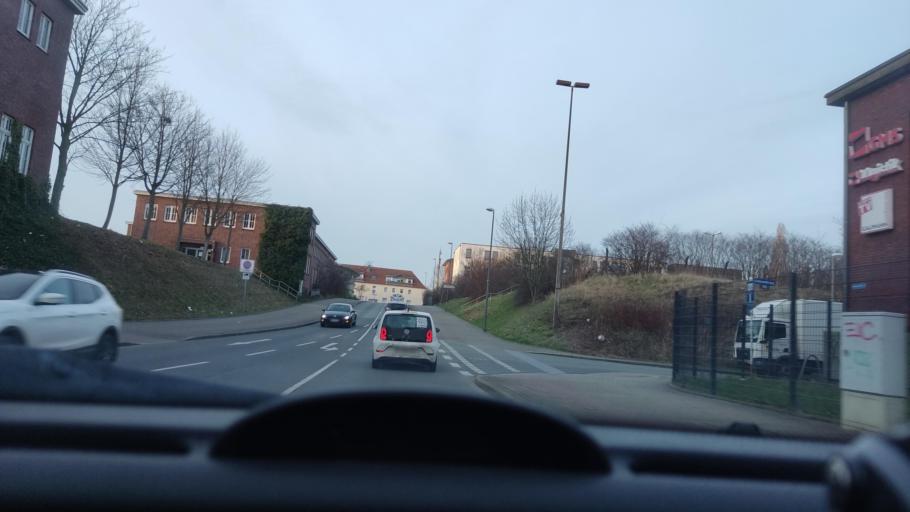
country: DE
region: North Rhine-Westphalia
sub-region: Regierungsbezirk Arnsberg
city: Dortmund
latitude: 51.5477
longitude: 7.4650
